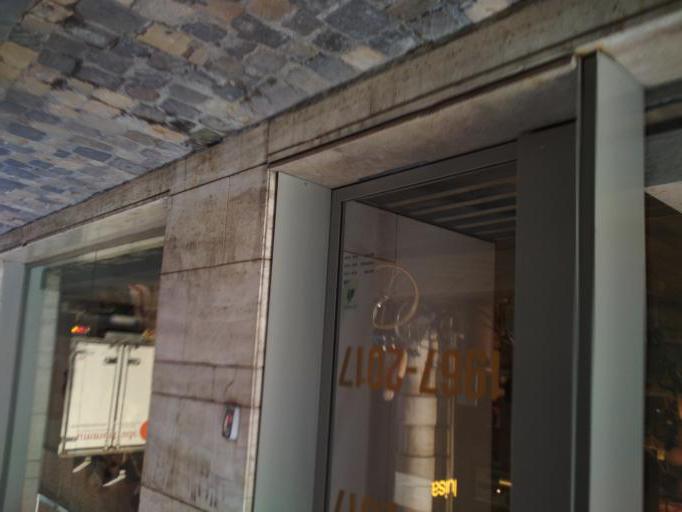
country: IT
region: Emilia-Romagna
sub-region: Provincia di Rimini
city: Rimini
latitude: 44.0615
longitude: 12.5675
